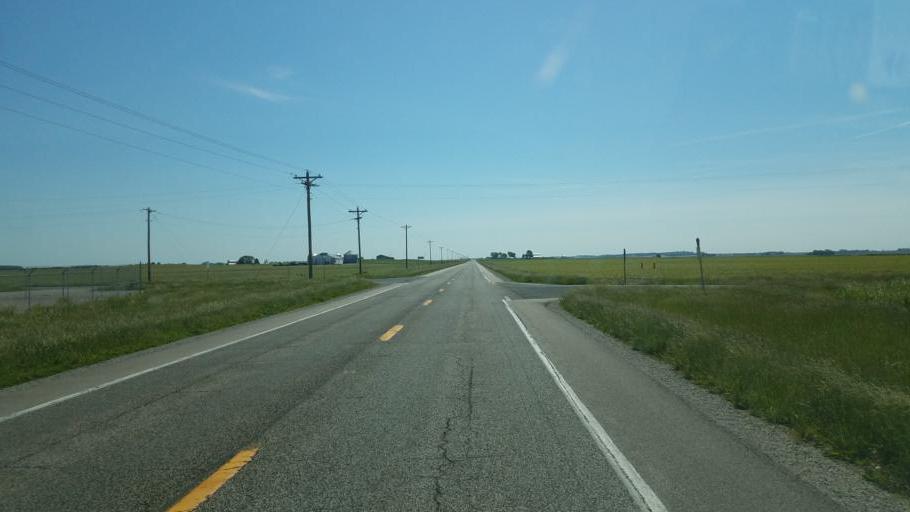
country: US
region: Illinois
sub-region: Mason County
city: Manito
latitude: 40.3037
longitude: -89.7727
